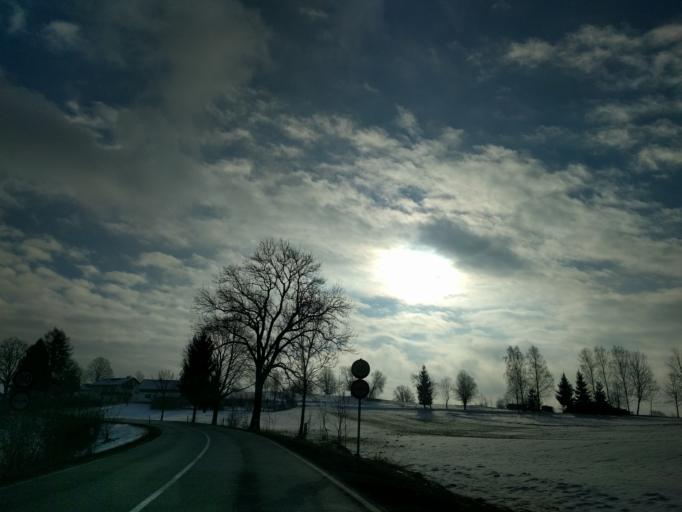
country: DE
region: Bavaria
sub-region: Lower Bavaria
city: Langdorf
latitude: 48.9878
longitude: 13.1703
